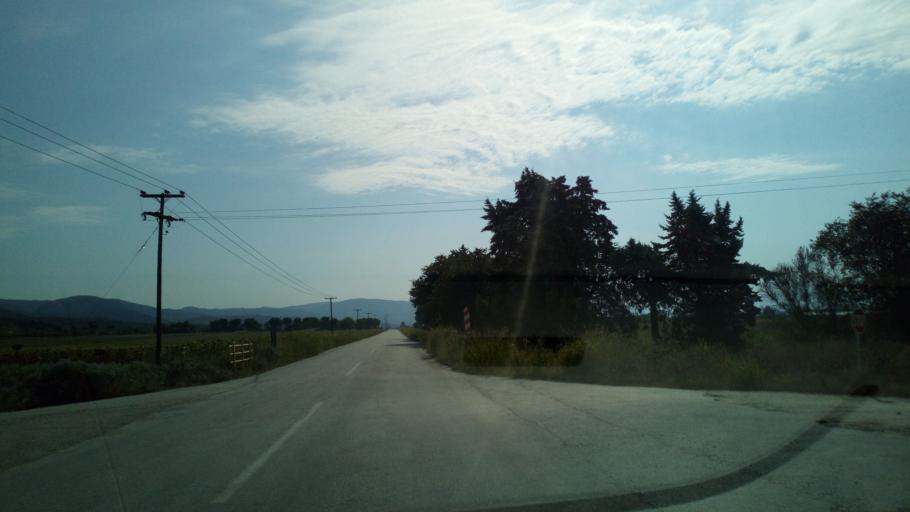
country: GR
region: Central Macedonia
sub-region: Nomos Thessalonikis
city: Askos
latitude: 40.6896
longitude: 23.3042
